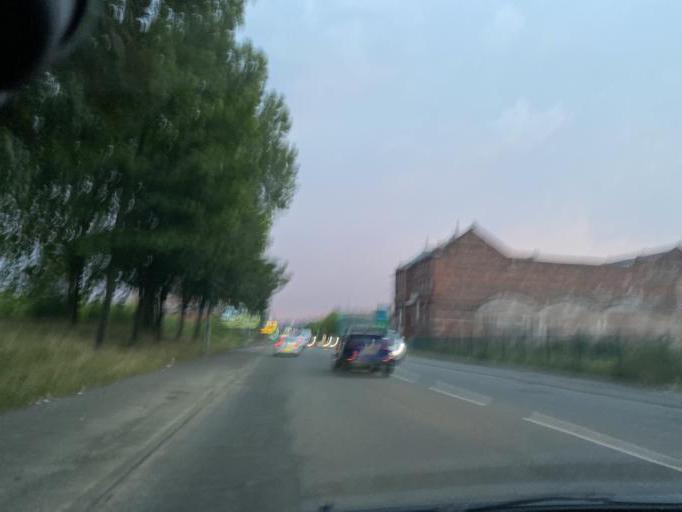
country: GB
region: England
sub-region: Manchester
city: Longsight
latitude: 53.4737
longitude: -2.1858
